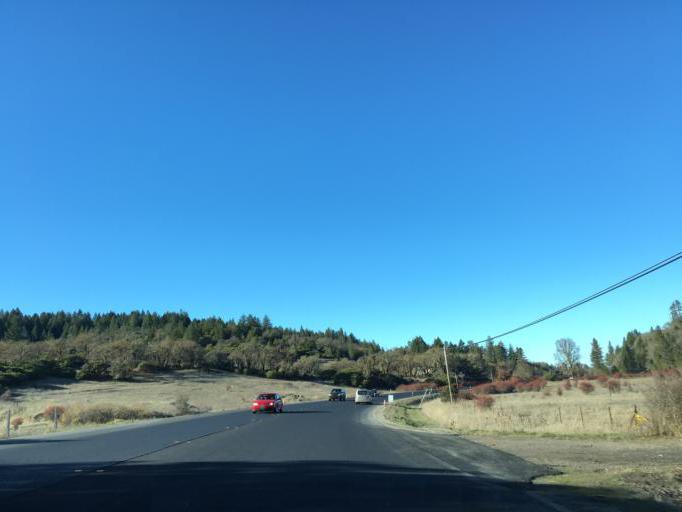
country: US
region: California
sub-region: Mendocino County
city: Laytonville
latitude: 39.6329
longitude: -123.4668
